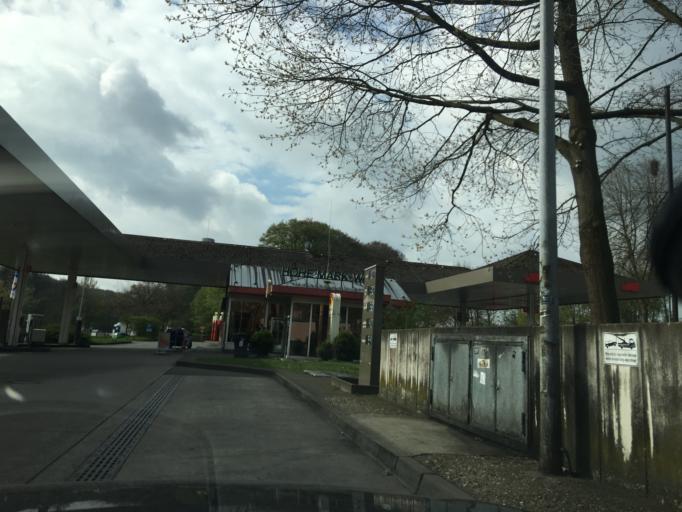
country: DE
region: North Rhine-Westphalia
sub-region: Regierungsbezirk Munster
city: Haltern
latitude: 51.7724
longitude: 7.1754
